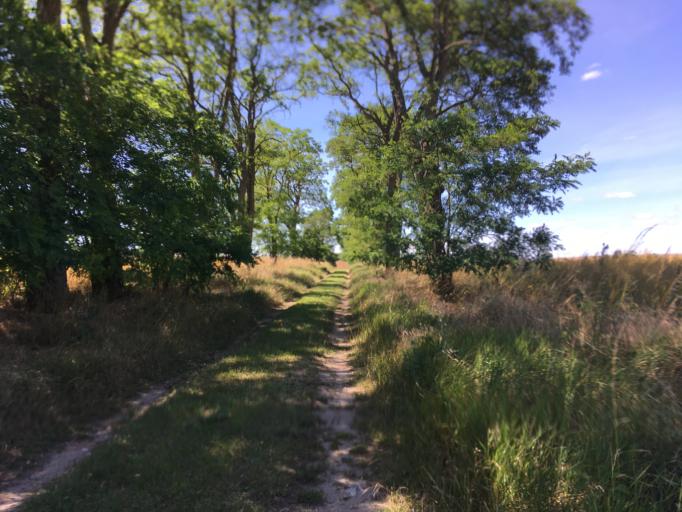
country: DE
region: Brandenburg
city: Brussow
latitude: 53.3262
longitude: 14.0817
